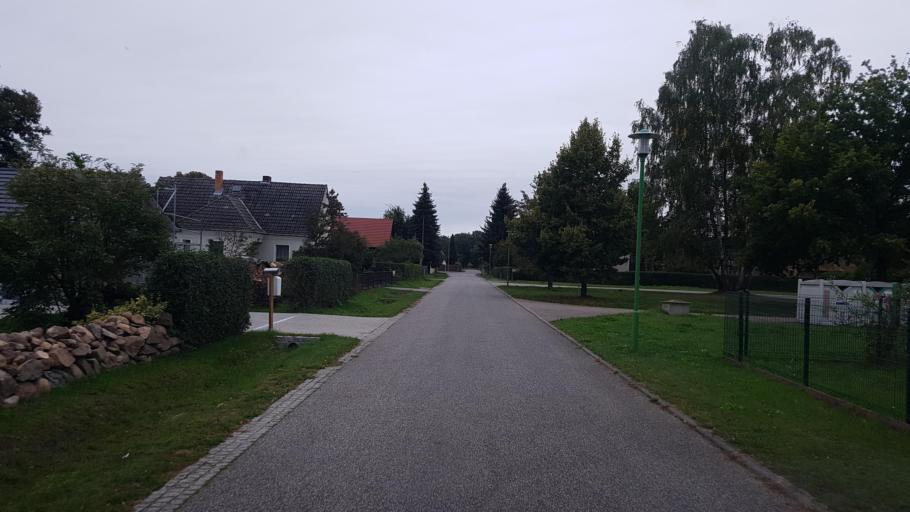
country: DE
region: Brandenburg
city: Golssen
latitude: 51.9721
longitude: 13.5630
